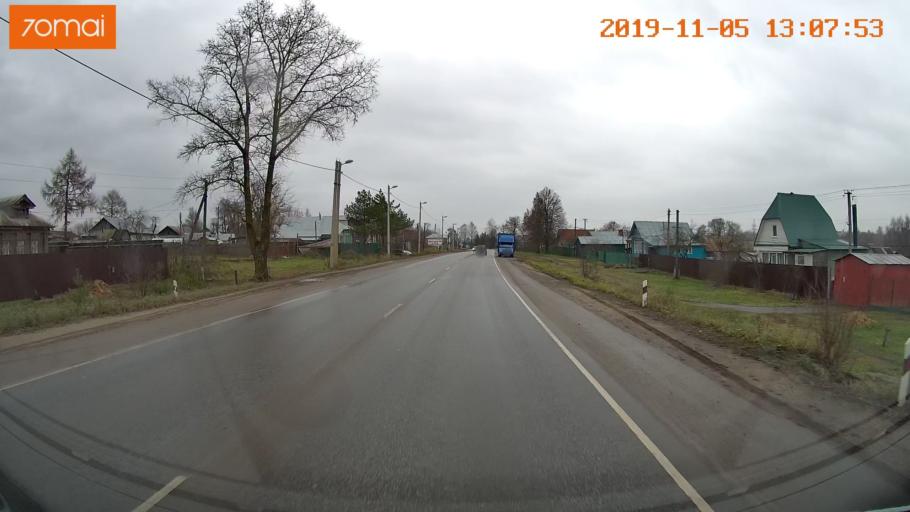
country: RU
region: Ivanovo
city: Kitovo
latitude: 56.8658
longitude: 41.2859
